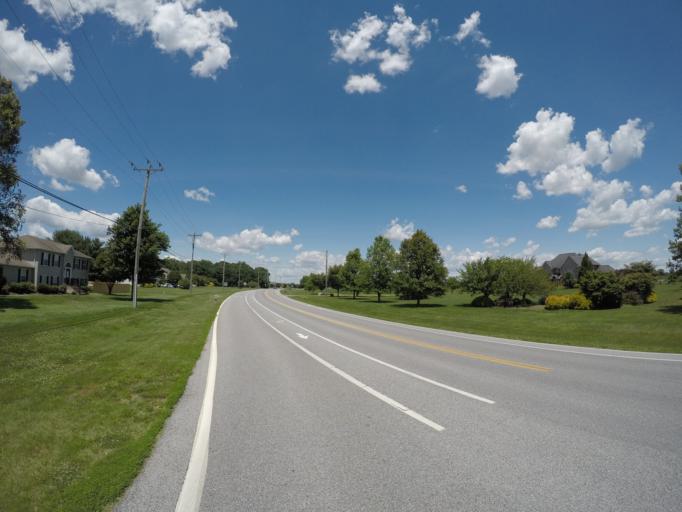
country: US
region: Delaware
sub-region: New Castle County
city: Middletown
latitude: 39.4798
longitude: -75.7362
